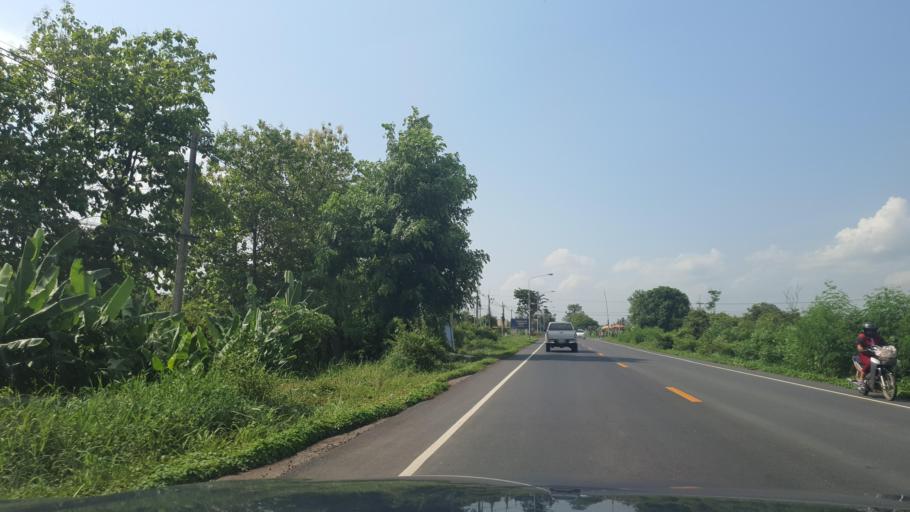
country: TH
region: Sukhothai
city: Si Samrong
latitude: 17.2125
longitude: 99.8496
